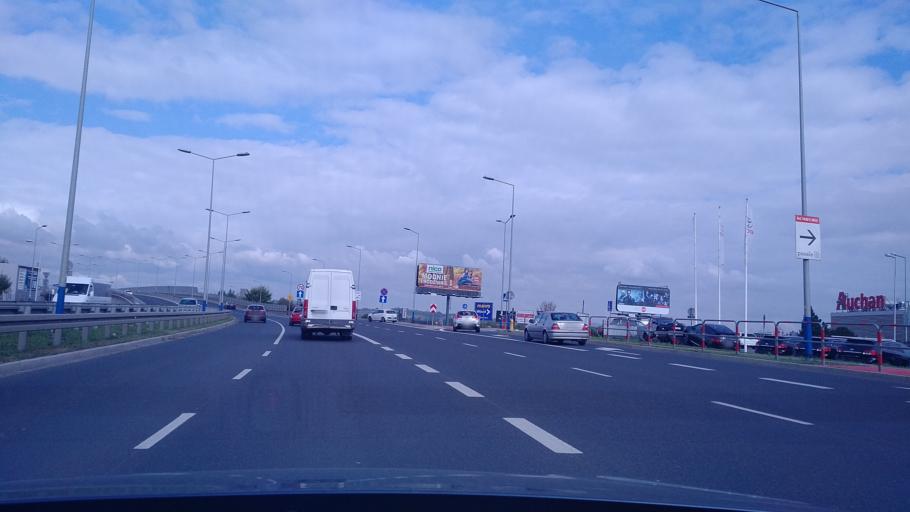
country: PL
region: Lesser Poland Voivodeship
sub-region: Powiat krakowski
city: Zielonki
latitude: 50.0916
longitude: 19.8934
